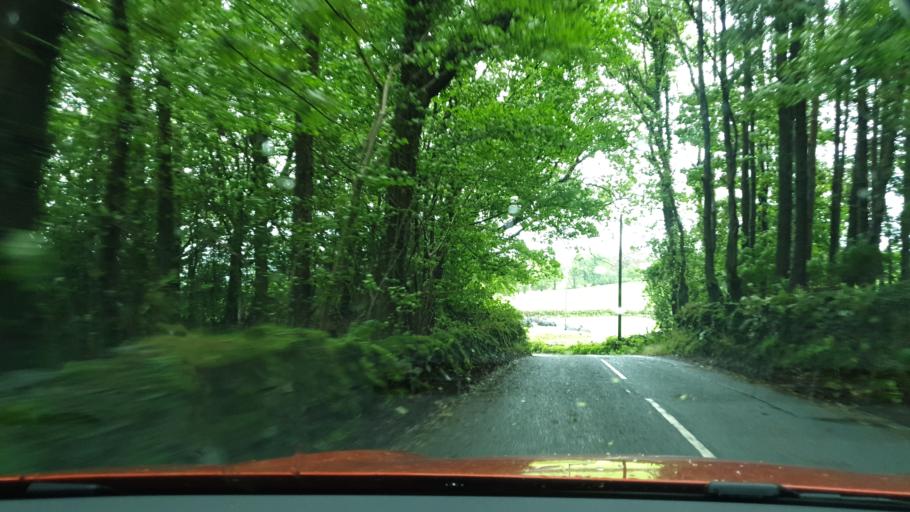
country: GB
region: England
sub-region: Cumbria
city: Ulverston
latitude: 54.2497
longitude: -3.0539
